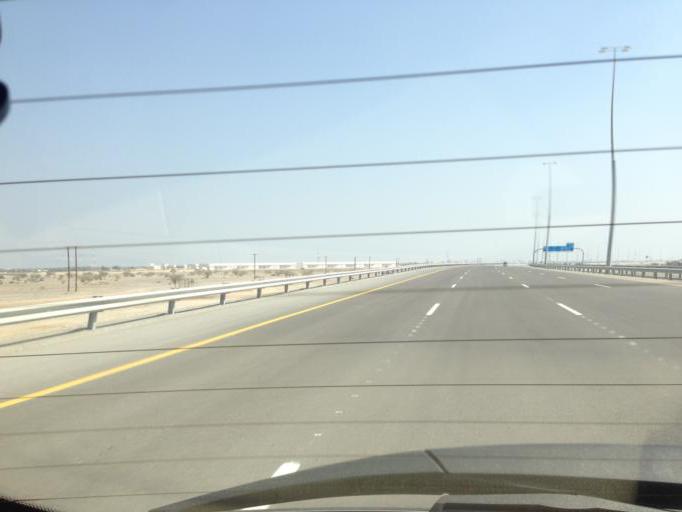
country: OM
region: Al Batinah
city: Barka'
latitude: 23.6258
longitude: 57.8468
